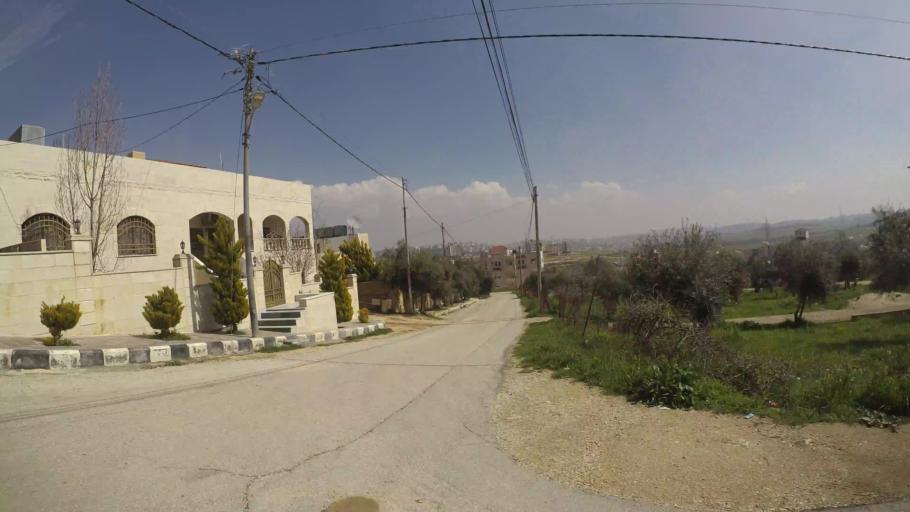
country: JO
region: Amman
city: Al Bunayyat ash Shamaliyah
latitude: 31.8871
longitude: 35.8971
